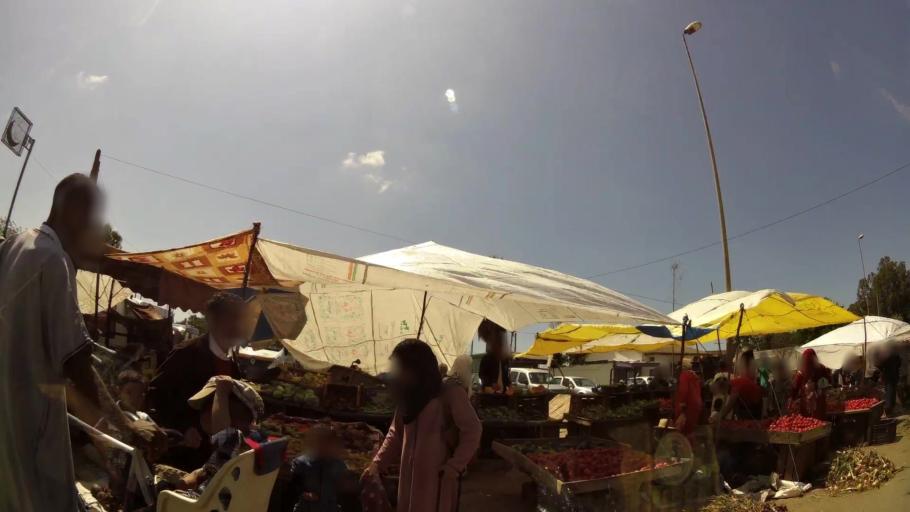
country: MA
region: Gharb-Chrarda-Beni Hssen
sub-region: Kenitra Province
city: Kenitra
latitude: 34.2308
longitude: -6.5342
